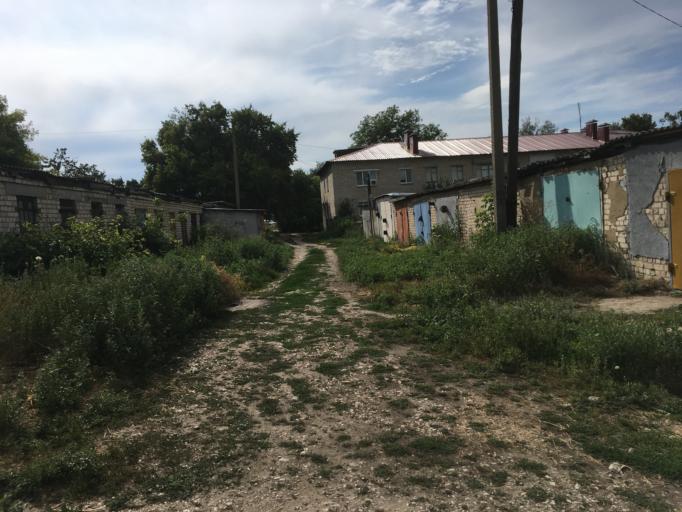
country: RU
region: Samara
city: Bezenchuk
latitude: 52.9873
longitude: 49.4433
